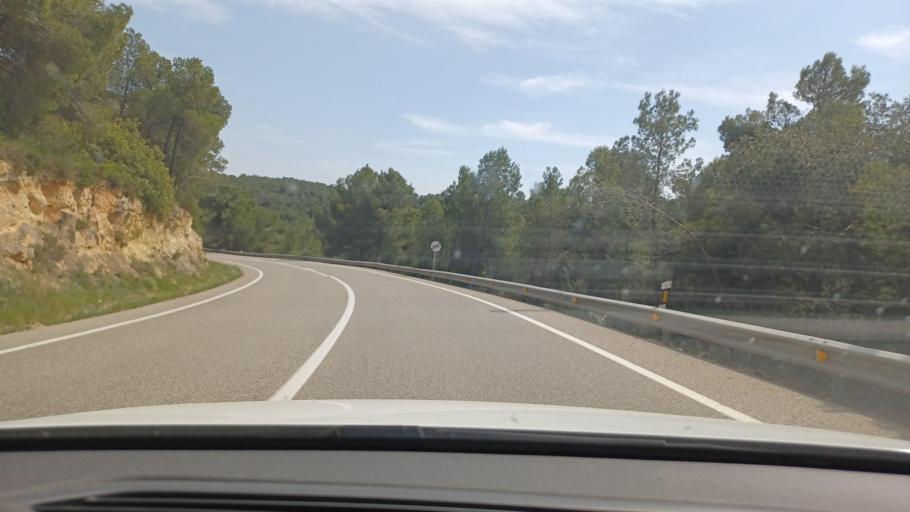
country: ES
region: Catalonia
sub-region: Provincia de Tarragona
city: Vilalba dels Arcs
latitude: 41.0864
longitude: 0.4157
